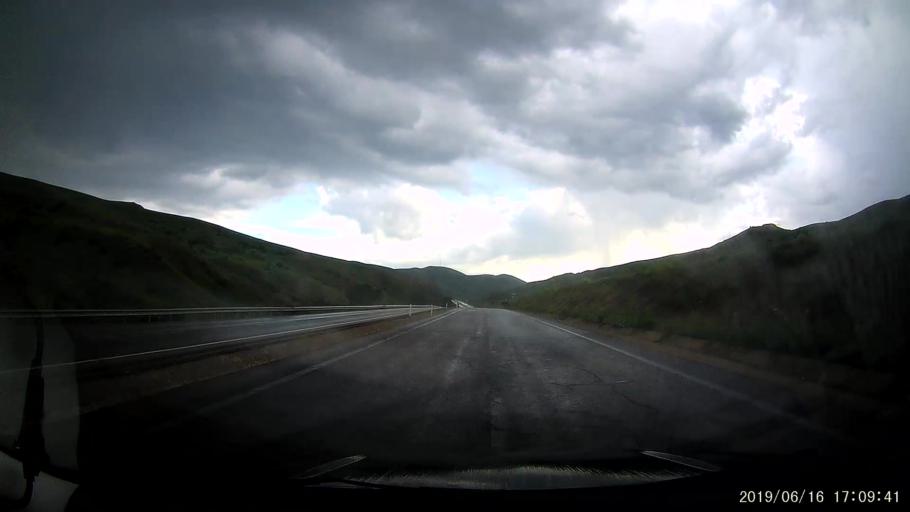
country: TR
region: Erzurum
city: Askale
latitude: 39.8911
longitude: 40.6481
